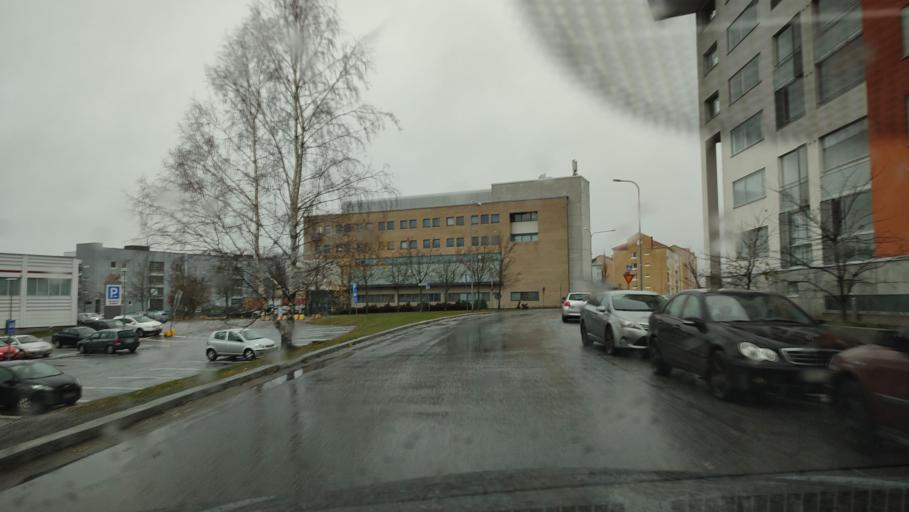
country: FI
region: Ostrobothnia
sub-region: Vaasa
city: Vaasa
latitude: 63.0921
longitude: 21.6322
